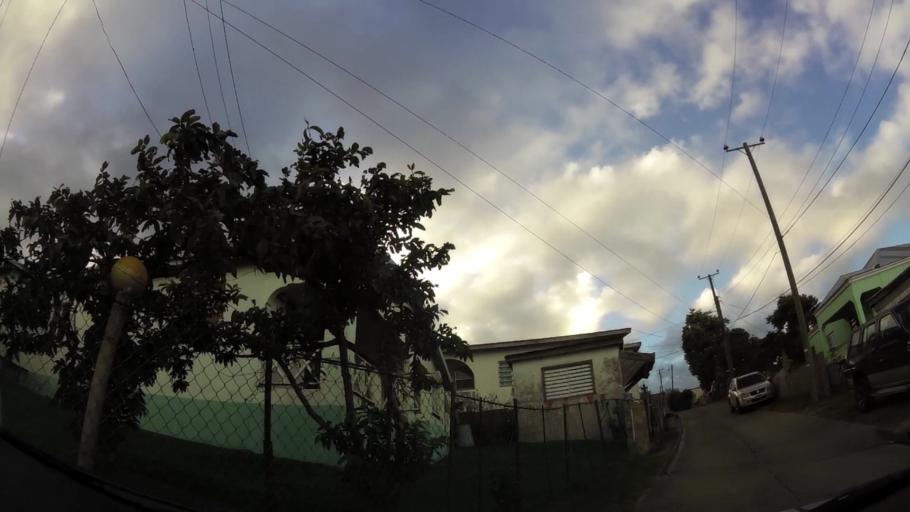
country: KN
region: Saint Mary Cayon
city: Cayon
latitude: 17.3482
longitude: -62.7309
